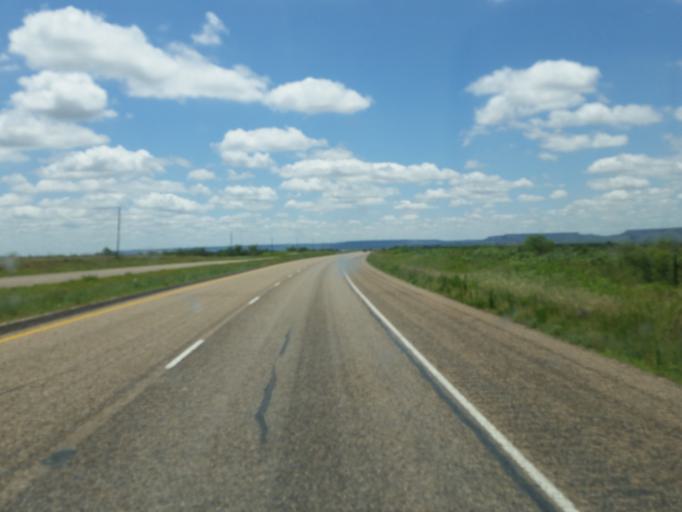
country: US
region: Texas
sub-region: Garza County
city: Post
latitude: 33.0888
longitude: -101.2441
